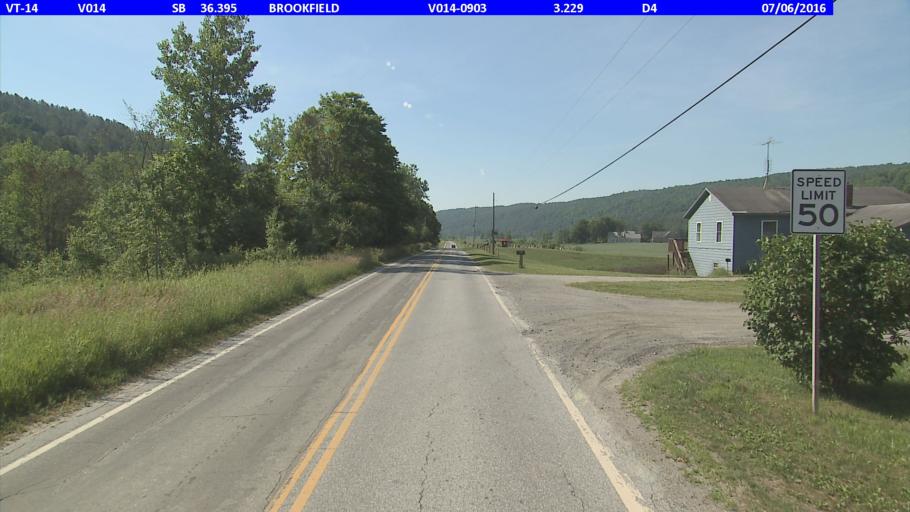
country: US
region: Vermont
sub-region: Orange County
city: Williamstown
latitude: 44.0236
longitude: -72.5713
